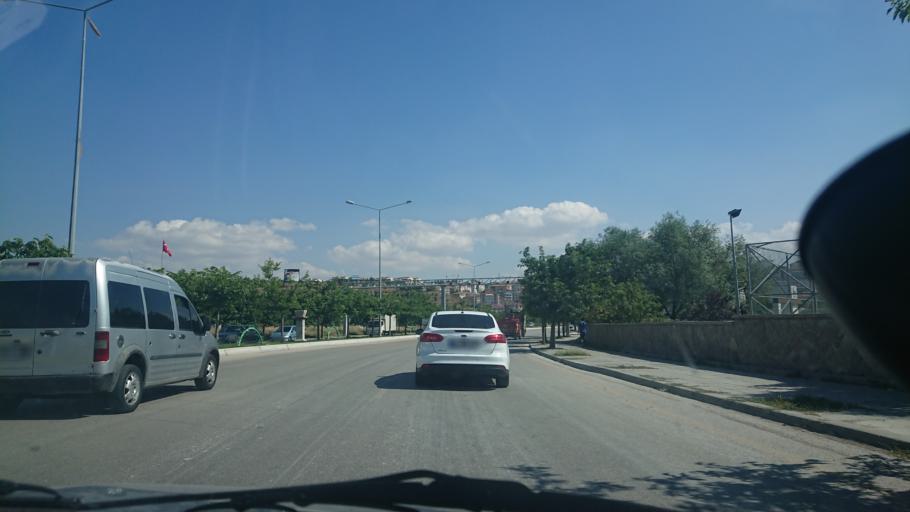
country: TR
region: Ankara
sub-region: Goelbasi
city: Golbasi
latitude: 39.8032
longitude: 32.8085
